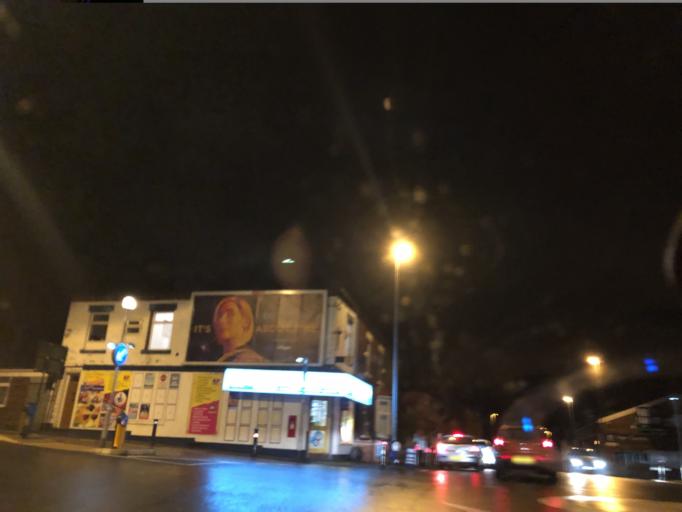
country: GB
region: England
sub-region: Borough of Oldham
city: Oldham
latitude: 53.5255
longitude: -2.1179
